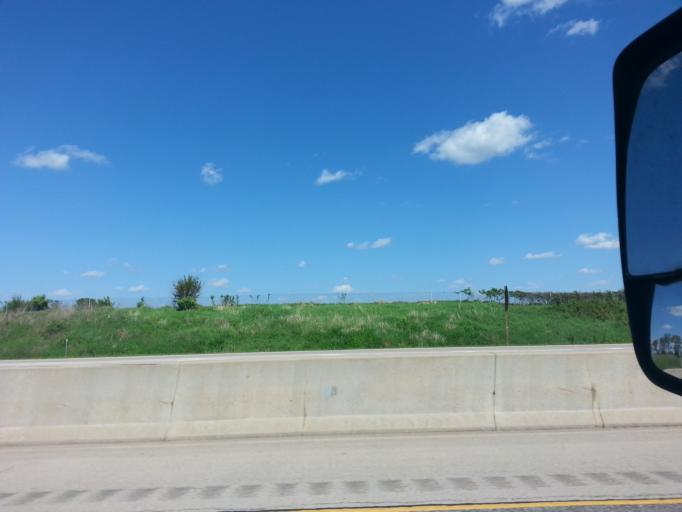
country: US
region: Illinois
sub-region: Winnebago County
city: Cherry Valley
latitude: 42.3144
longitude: -88.9647
